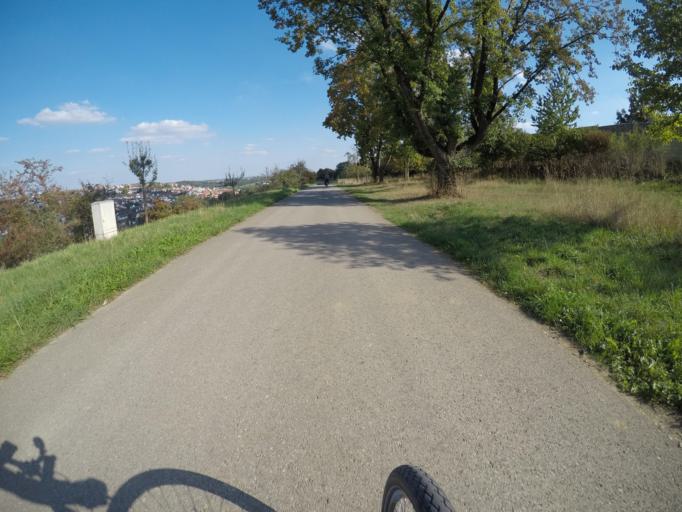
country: DE
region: Baden-Wuerttemberg
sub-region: Regierungsbezirk Stuttgart
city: Denkendorf
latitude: 48.6944
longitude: 9.3033
